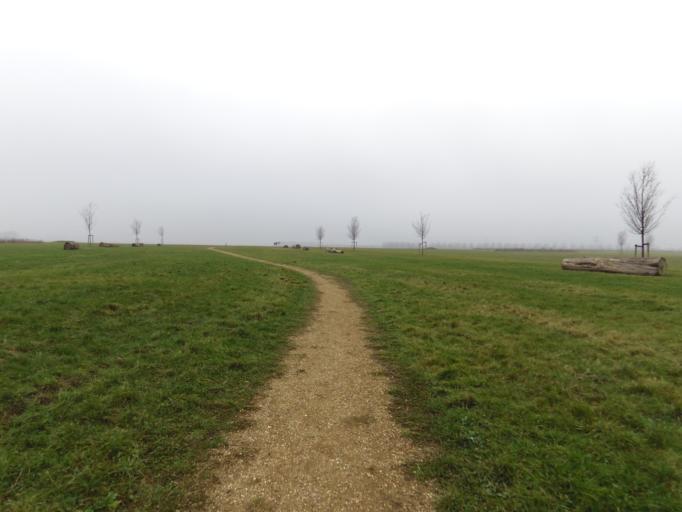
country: NL
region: South Holland
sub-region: Gemeente Oud-Beijerland
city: Oud-Beijerland
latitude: 51.8361
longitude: 4.3844
